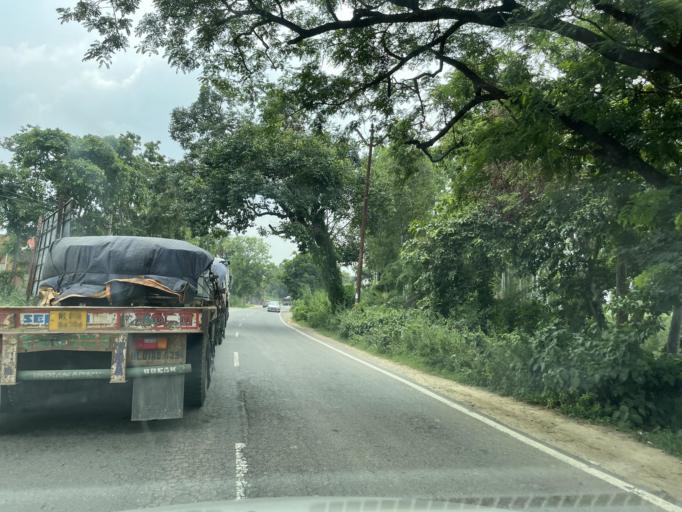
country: IN
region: Uttar Pradesh
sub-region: Bijnor
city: Najibabad
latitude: 29.5878
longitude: 78.3386
